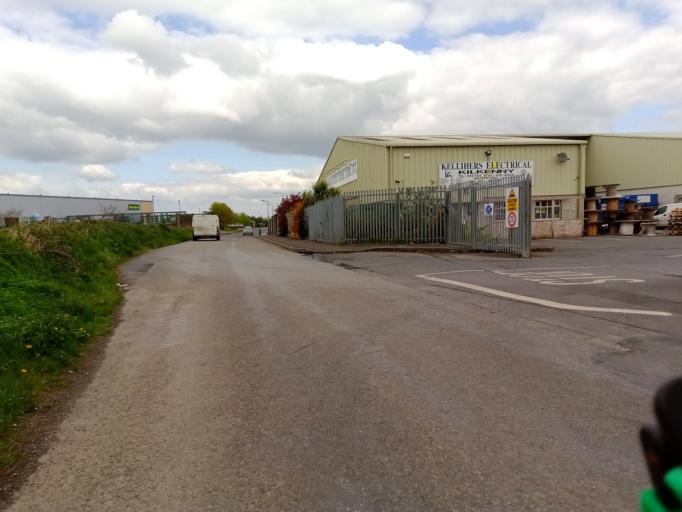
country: IE
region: Leinster
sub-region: Kilkenny
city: Kilkenny
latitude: 52.6331
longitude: -7.2423
